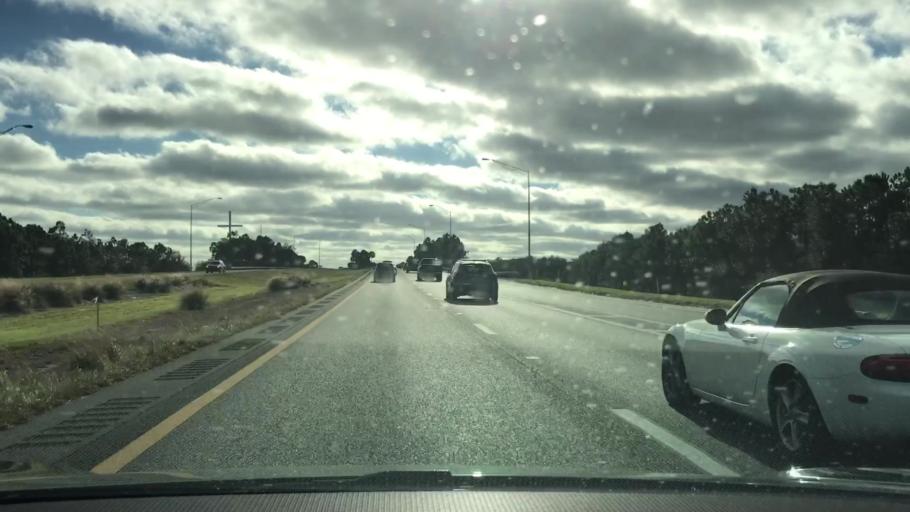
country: US
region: Florida
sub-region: Orange County
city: Hunters Creek
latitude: 28.3693
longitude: -81.4302
